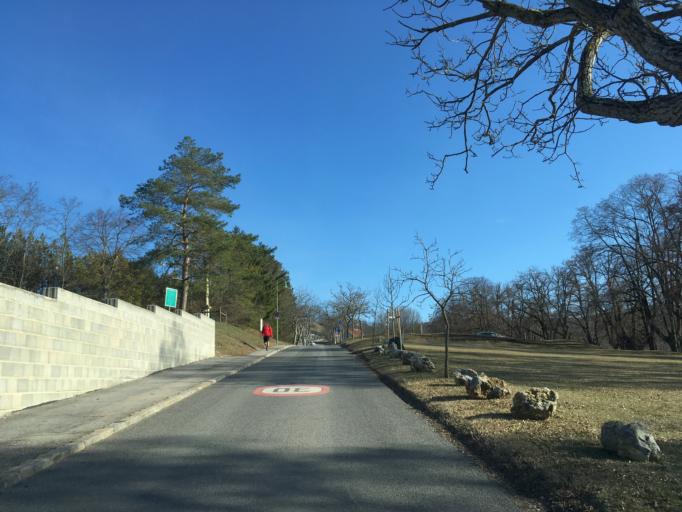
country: AT
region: Burgenland
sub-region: Eisenstadt-Umgebung
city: Hornstein
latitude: 47.8784
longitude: 16.4497
